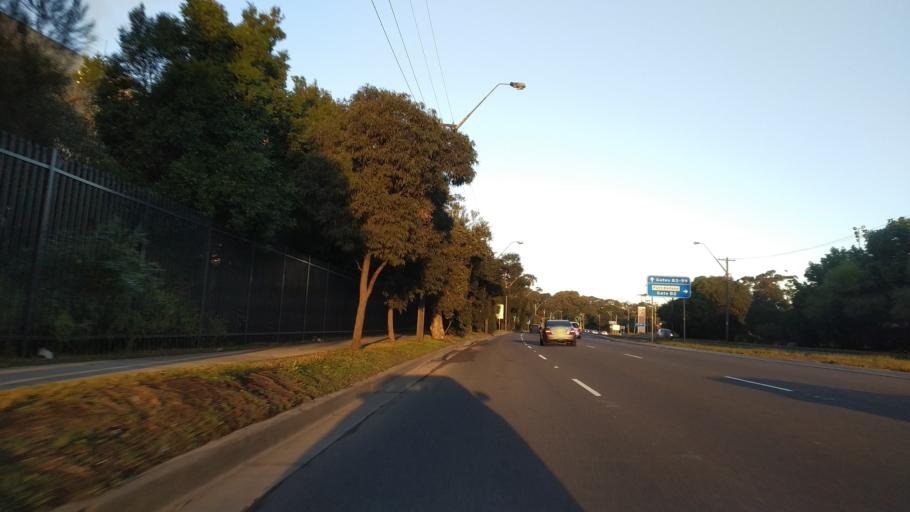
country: AU
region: New South Wales
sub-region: Randwick
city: Maroubra
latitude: -33.9644
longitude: 151.2228
